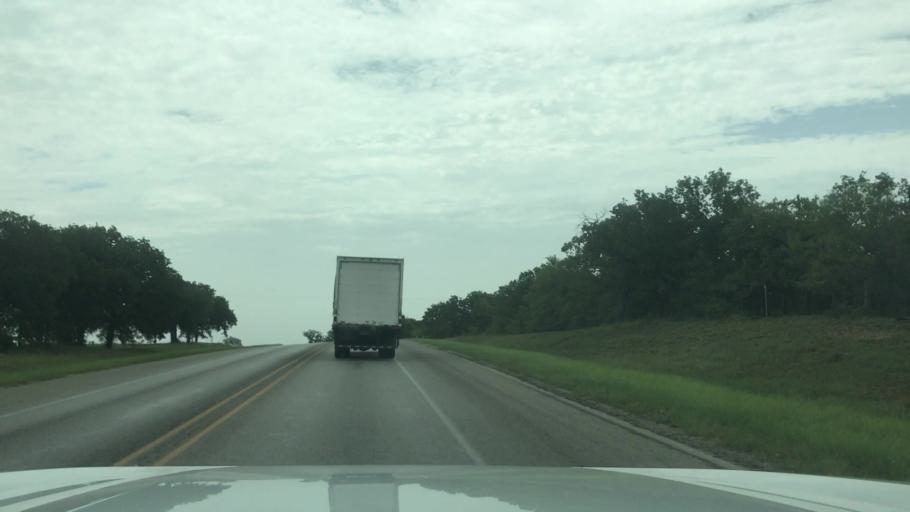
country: US
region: Texas
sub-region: Comanche County
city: De Leon
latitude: 32.1062
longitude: -98.4901
